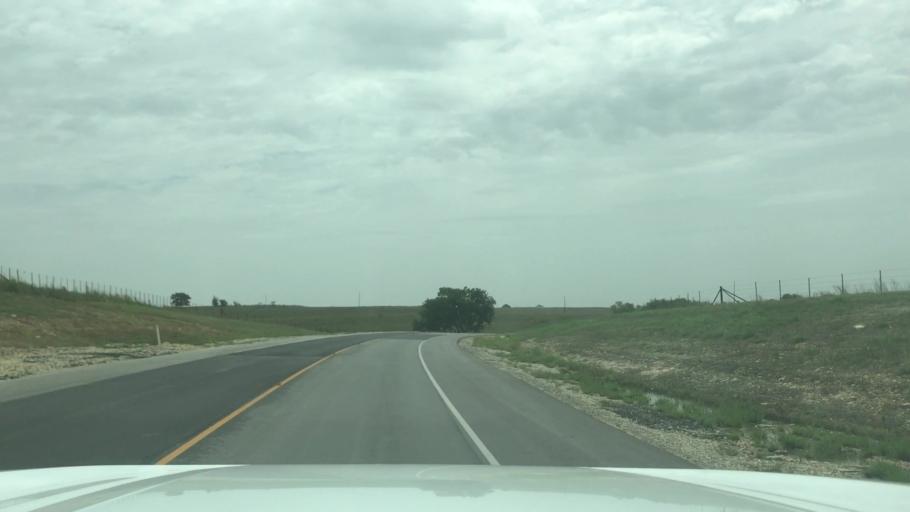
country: US
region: Texas
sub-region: Erath County
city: Dublin
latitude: 32.0728
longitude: -98.2244
